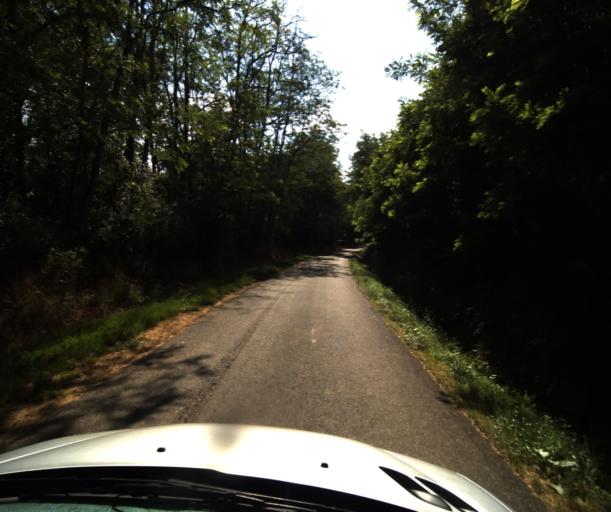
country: FR
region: Midi-Pyrenees
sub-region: Departement du Tarn-et-Garonne
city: Finhan
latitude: 43.9004
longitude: 1.2680
